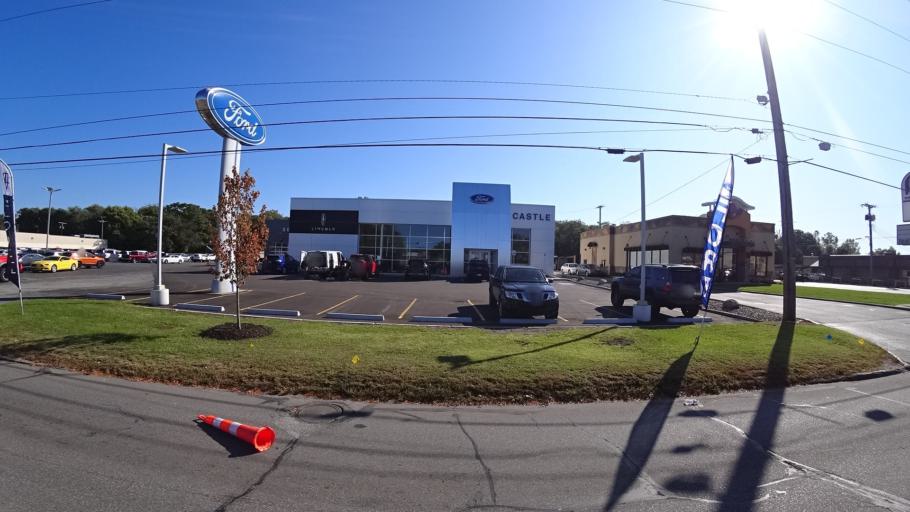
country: US
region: Indiana
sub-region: LaPorte County
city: Michigan City
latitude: 41.6832
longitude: -86.8939
